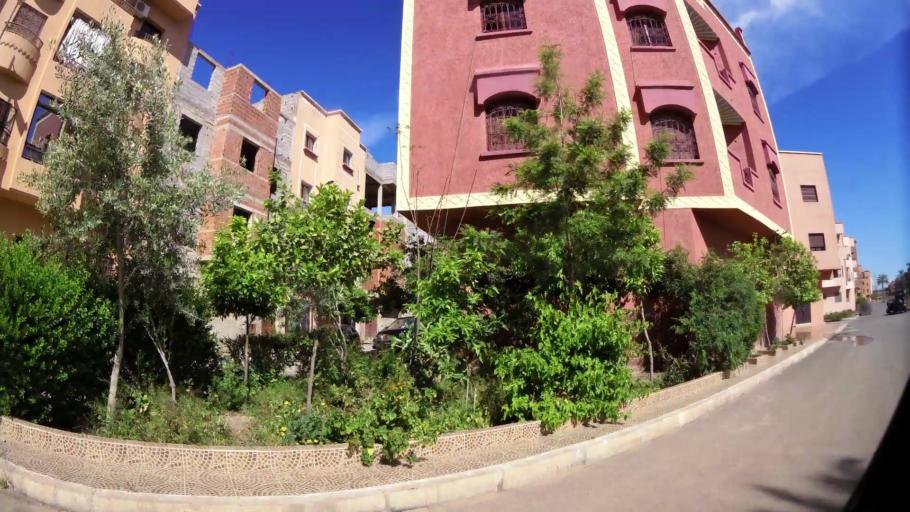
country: MA
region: Marrakech-Tensift-Al Haouz
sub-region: Marrakech
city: Marrakesh
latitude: 31.6709
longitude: -8.0250
